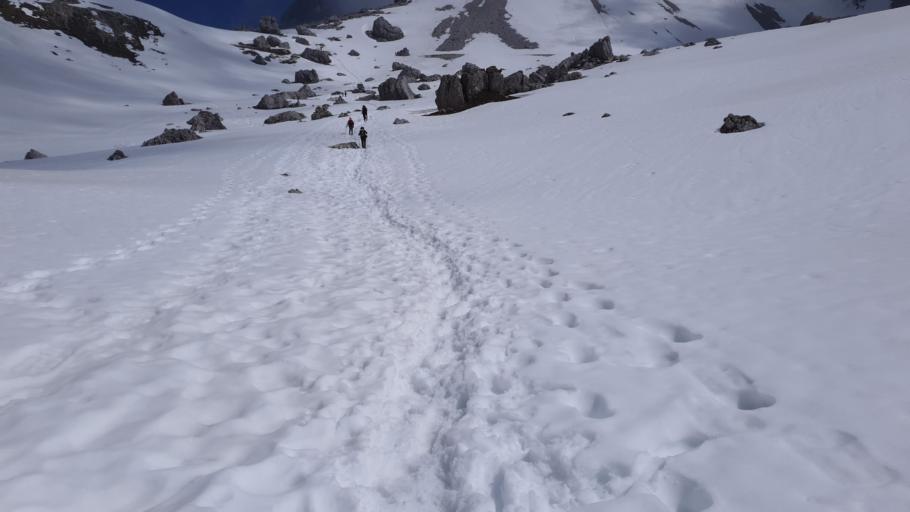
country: IT
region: Trentino-Alto Adige
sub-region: Bolzano
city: Sesto
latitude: 46.6193
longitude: 12.3124
